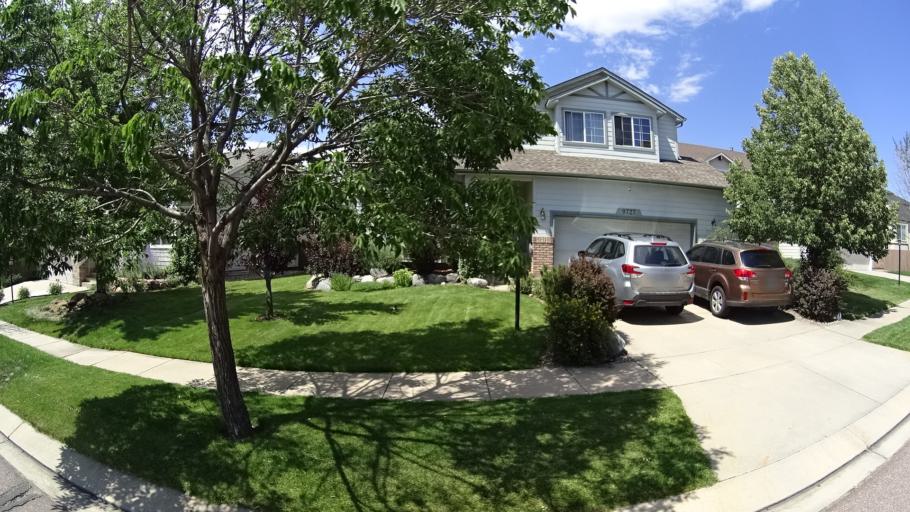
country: US
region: Colorado
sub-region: El Paso County
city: Black Forest
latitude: 38.9676
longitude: -104.7627
